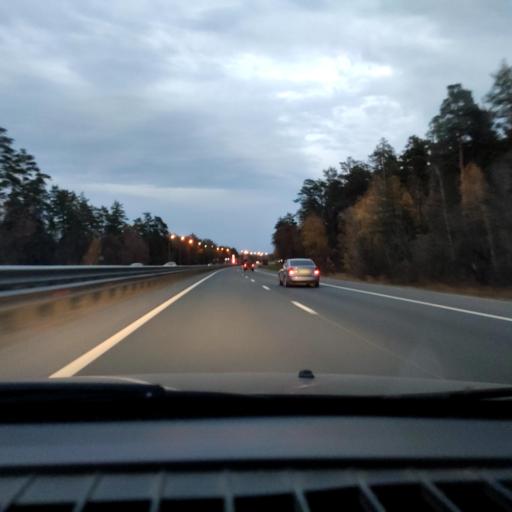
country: RU
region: Samara
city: Zhigulevsk
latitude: 53.5111
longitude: 49.5679
